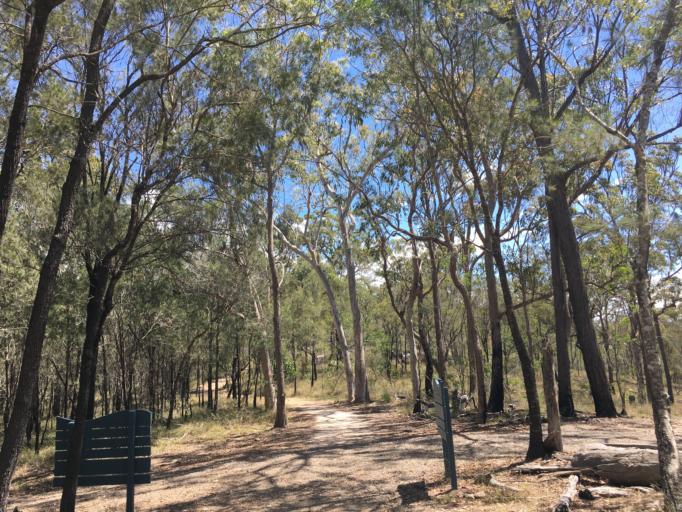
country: AU
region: Queensland
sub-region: Logan
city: Woodridge
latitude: -27.6261
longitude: 153.0856
